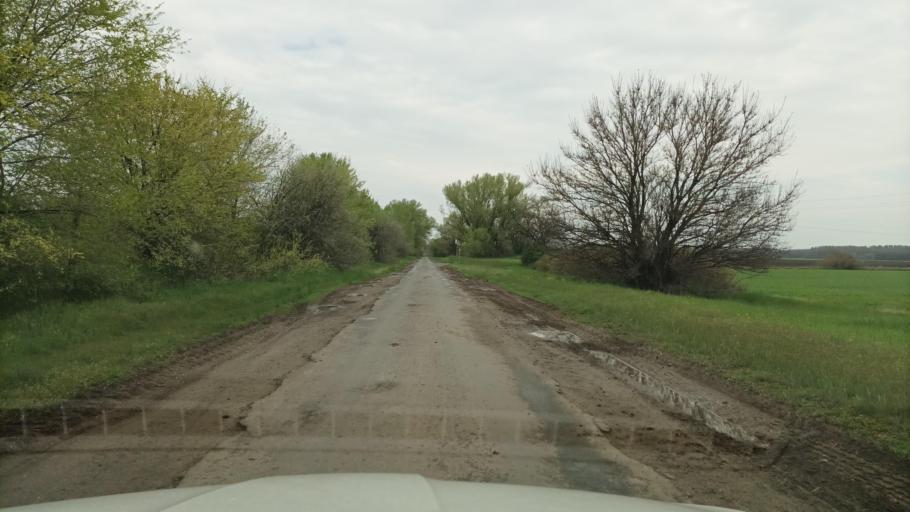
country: HU
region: Pest
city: Nagykoros
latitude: 46.9845
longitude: 19.8057
